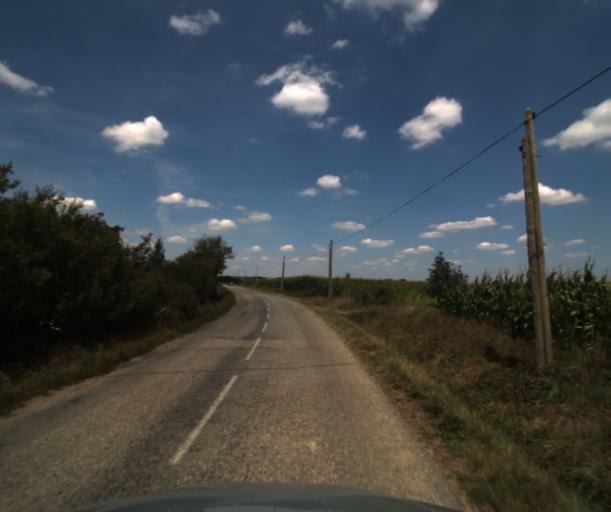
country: FR
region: Midi-Pyrenees
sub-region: Departement de la Haute-Garonne
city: Saint-Lys
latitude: 43.4953
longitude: 1.1787
